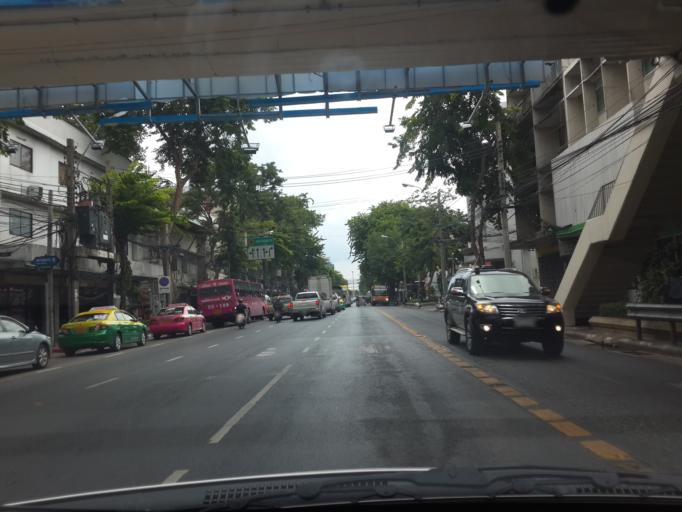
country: TH
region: Bangkok
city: Pom Prap Sattru Phai
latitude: 13.7565
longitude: 100.5112
